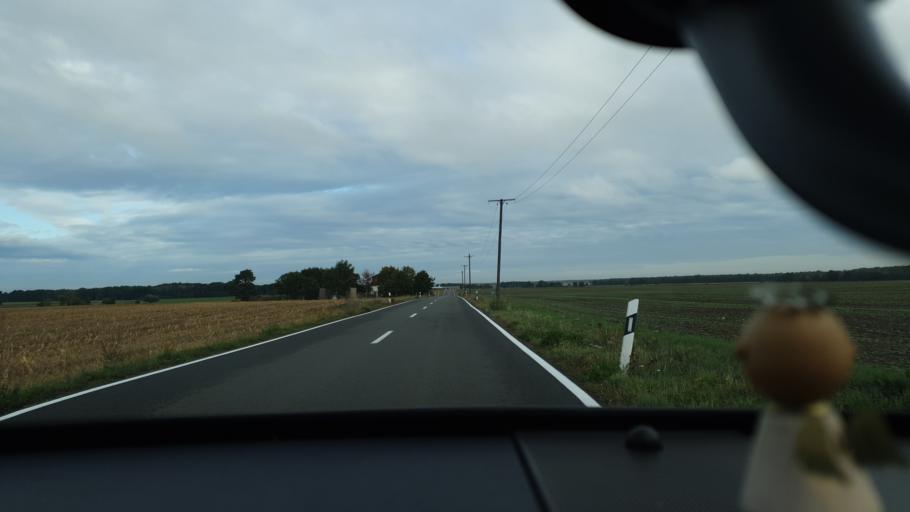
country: DE
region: Saxony
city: Schildau
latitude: 51.4640
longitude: 12.9274
